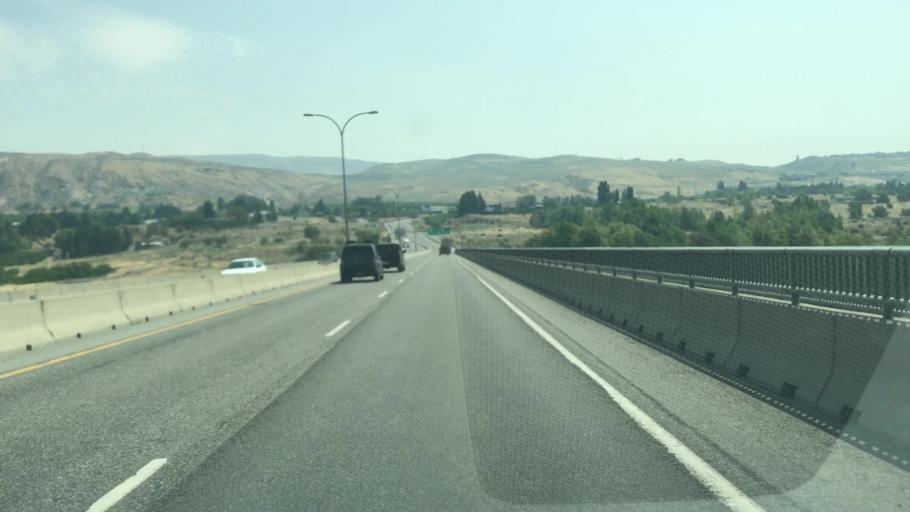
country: US
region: Washington
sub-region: Chelan County
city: Sunnyslope
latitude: 47.4713
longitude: -120.3175
